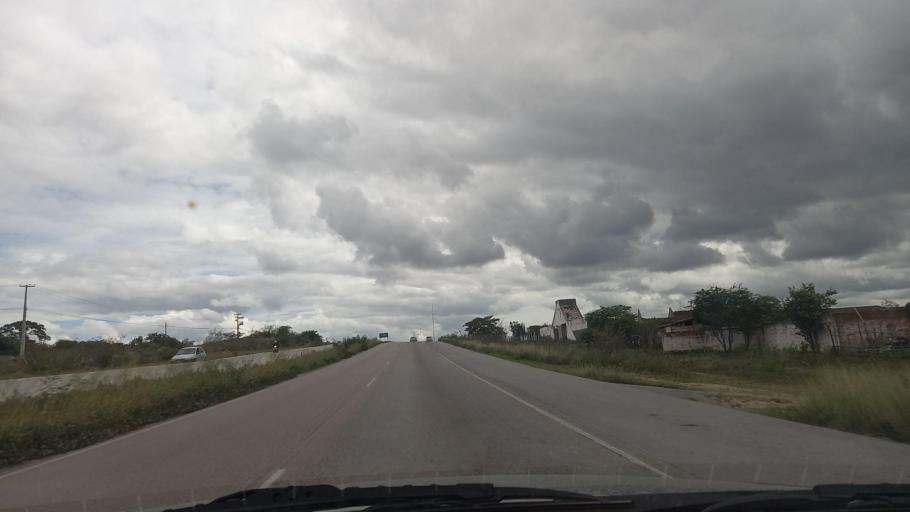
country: BR
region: Pernambuco
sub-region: Caruaru
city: Caruaru
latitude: -8.3279
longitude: -36.1186
